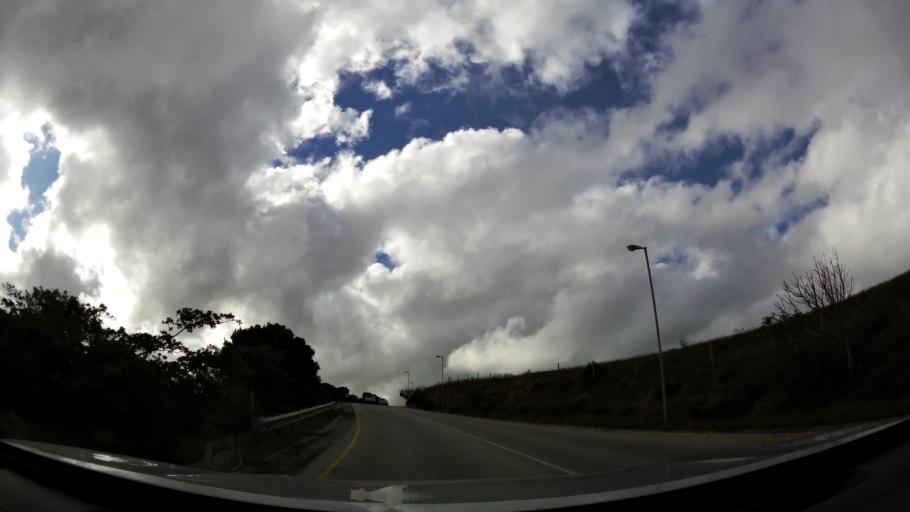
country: ZA
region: Western Cape
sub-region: Eden District Municipality
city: Knysna
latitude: -34.0735
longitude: 23.0850
